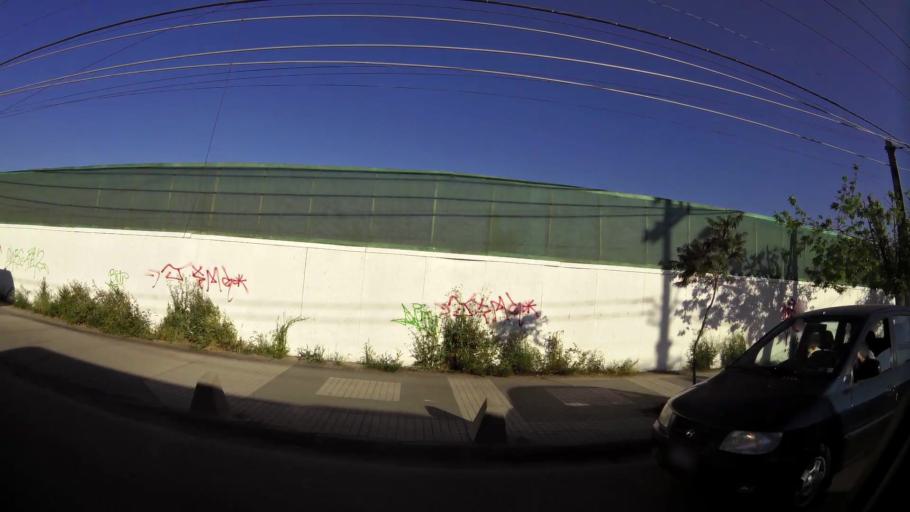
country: CL
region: Santiago Metropolitan
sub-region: Provincia de Talagante
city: Penaflor
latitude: -33.6084
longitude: -70.8561
